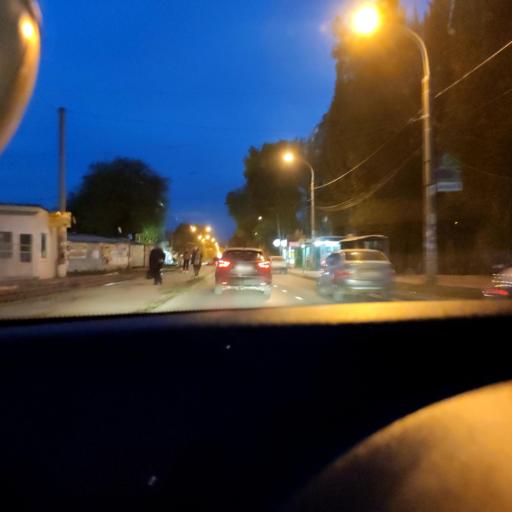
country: RU
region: Samara
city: Samara
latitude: 53.2451
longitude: 50.2508
